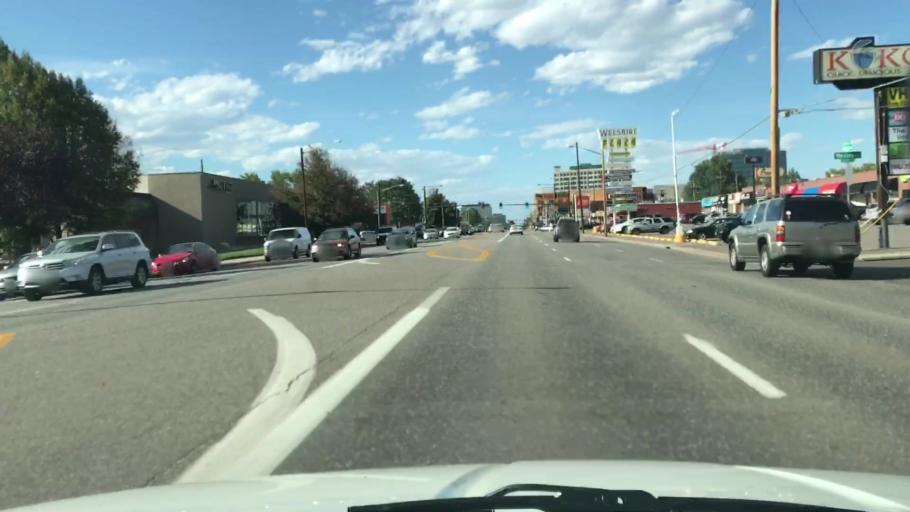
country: US
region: Colorado
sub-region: Arapahoe County
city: Glendale
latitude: 39.6732
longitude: -104.9407
